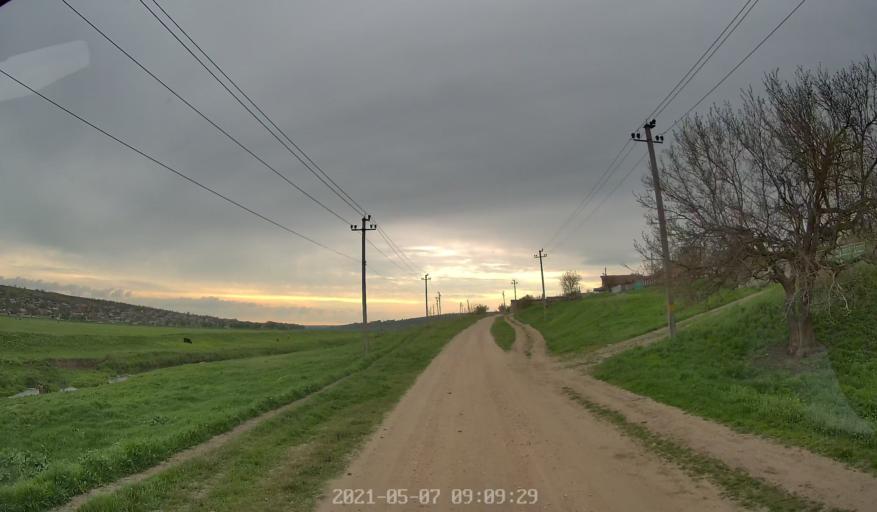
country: MD
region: Chisinau
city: Vadul lui Voda
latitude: 47.1192
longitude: 29.0042
